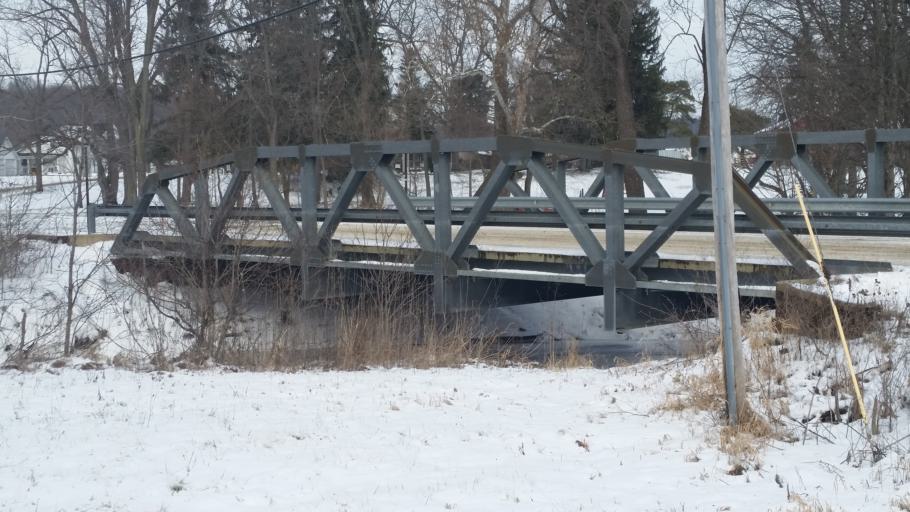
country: US
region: Ohio
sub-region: Knox County
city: Fredericktown
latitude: 40.4607
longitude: -82.6282
